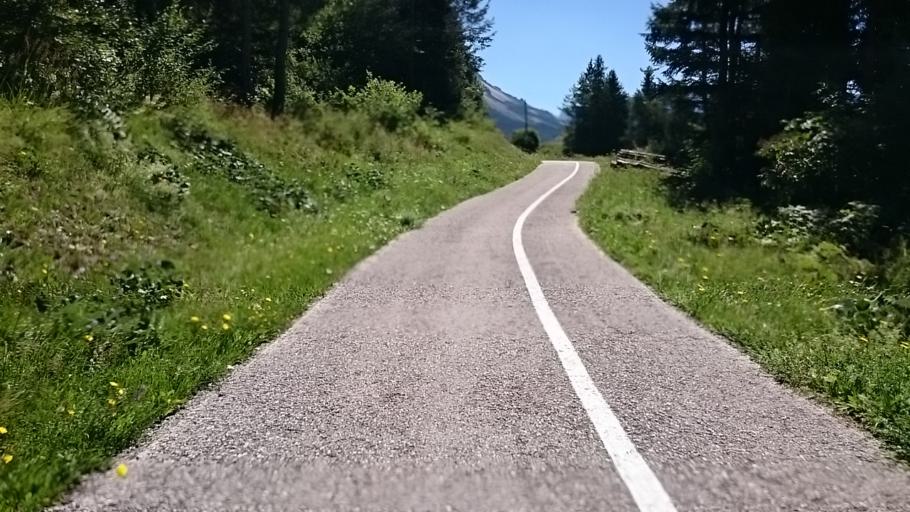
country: IT
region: Veneto
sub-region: Provincia di Belluno
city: San Vito
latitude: 46.4805
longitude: 12.1948
